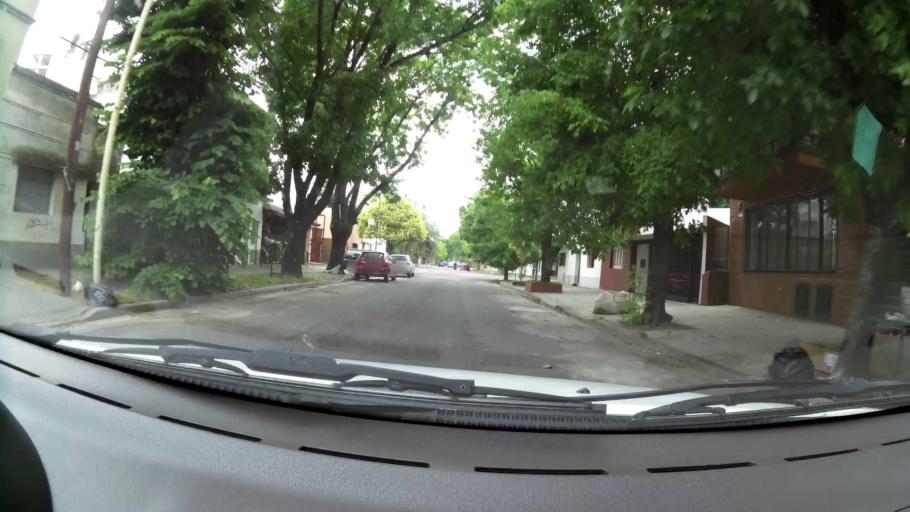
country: AR
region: Buenos Aires
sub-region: Partido de La Plata
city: La Plata
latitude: -34.9335
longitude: -57.9648
